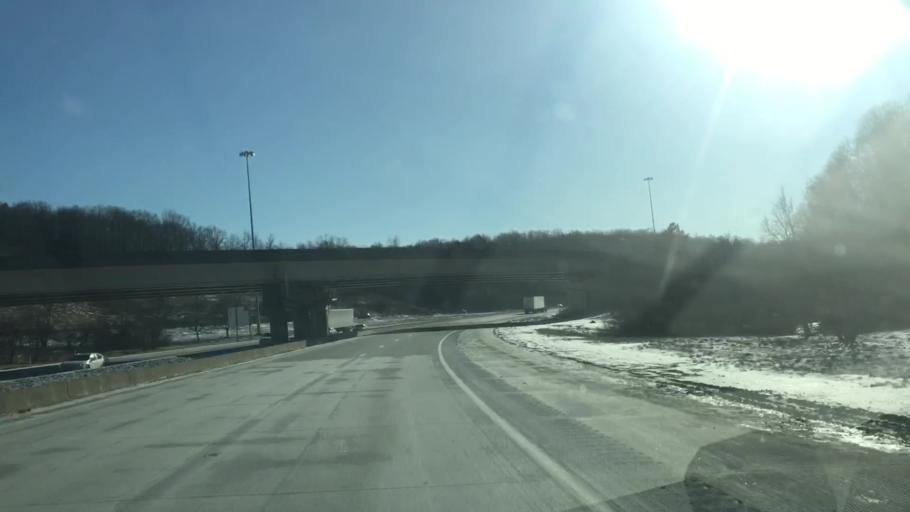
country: US
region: Pennsylvania
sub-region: Allegheny County
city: Enlow
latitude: 40.4665
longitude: -80.2002
